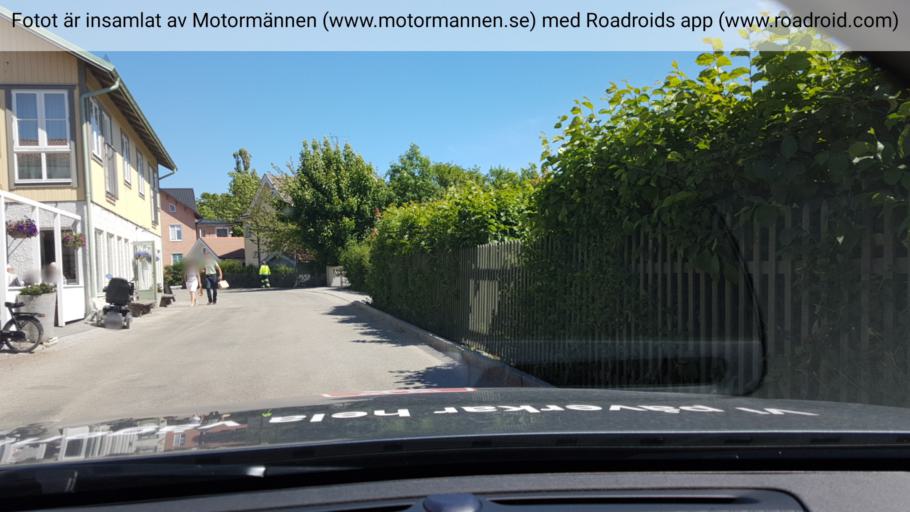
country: SE
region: Stockholm
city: Dalaro
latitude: 59.1315
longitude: 18.4066
